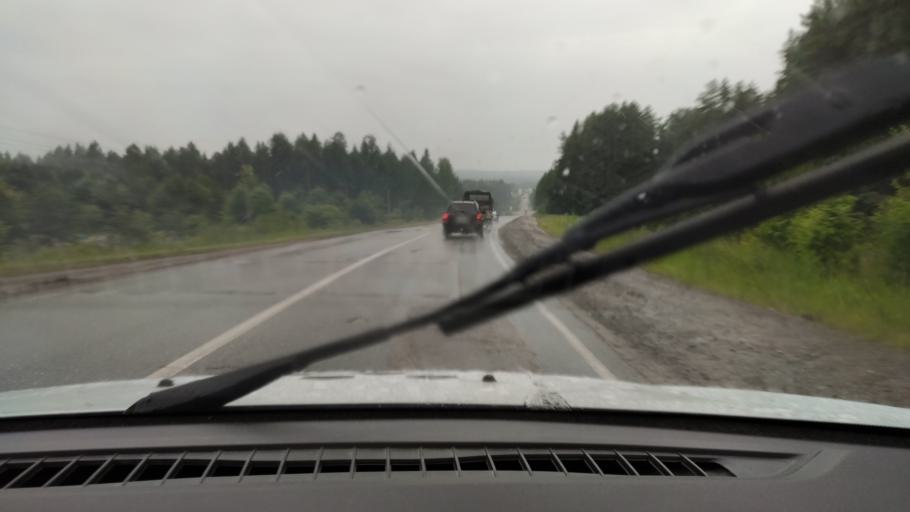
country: RU
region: Udmurtiya
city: Votkinsk
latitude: 57.0724
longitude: 54.0367
